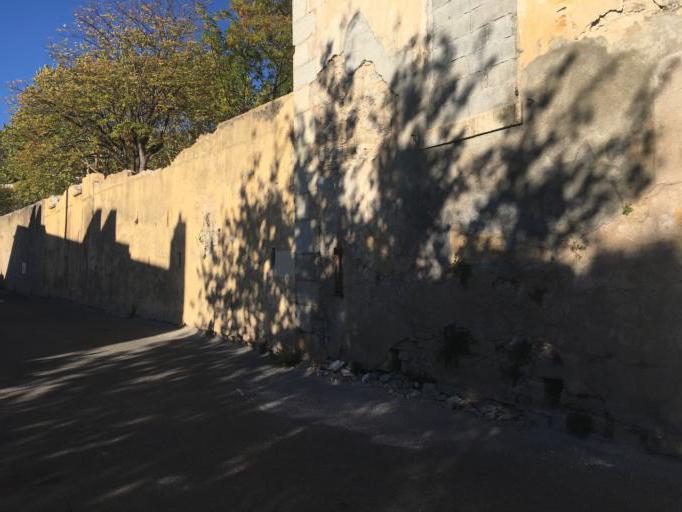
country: FR
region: Provence-Alpes-Cote d'Azur
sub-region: Departement du Var
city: Draguignan
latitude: 43.5419
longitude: 6.4637
